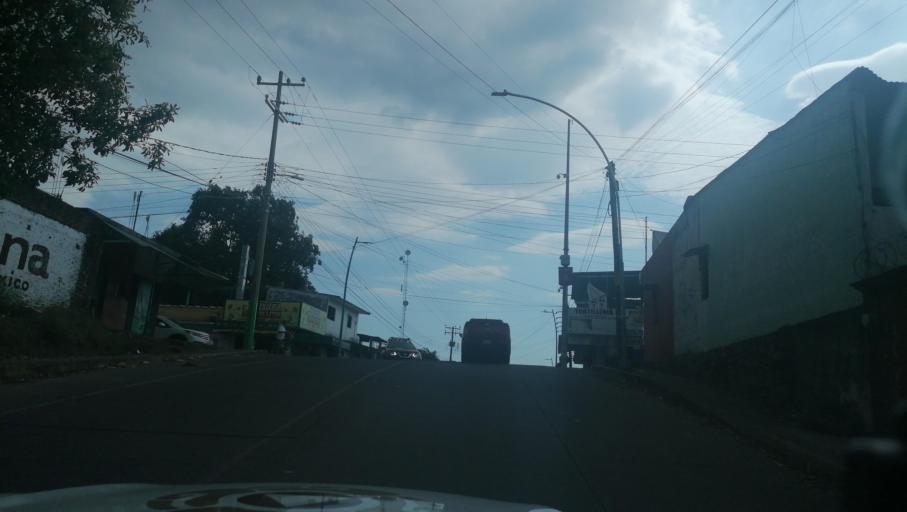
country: MX
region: Chiapas
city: Tapachula
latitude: 14.9265
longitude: -92.2532
